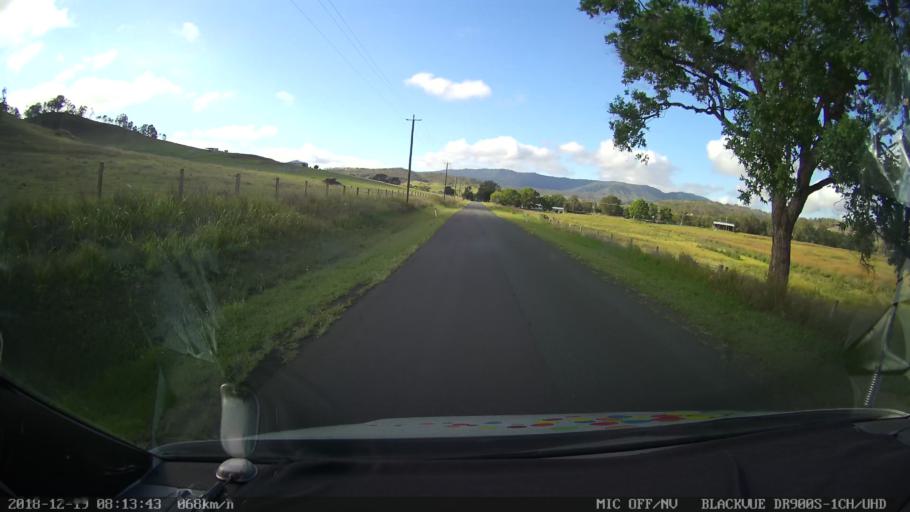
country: AU
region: Queensland
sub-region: Logan
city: Cedar Vale
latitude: -28.2414
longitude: 152.8902
